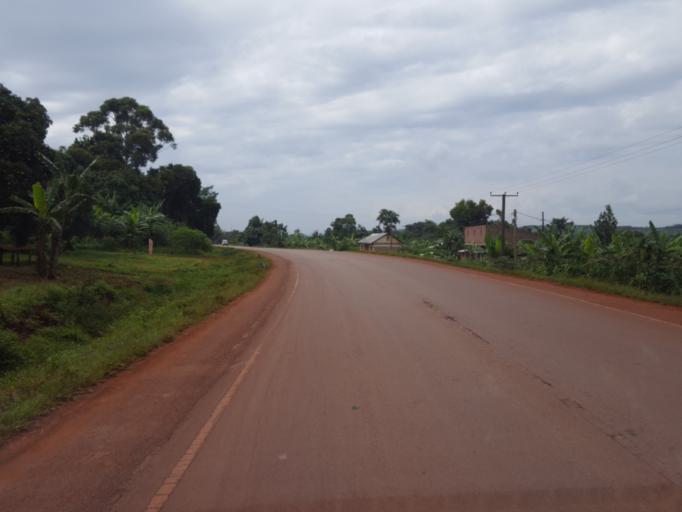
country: UG
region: Central Region
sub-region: Mityana District
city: Mityana
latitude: 0.6386
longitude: 32.1003
